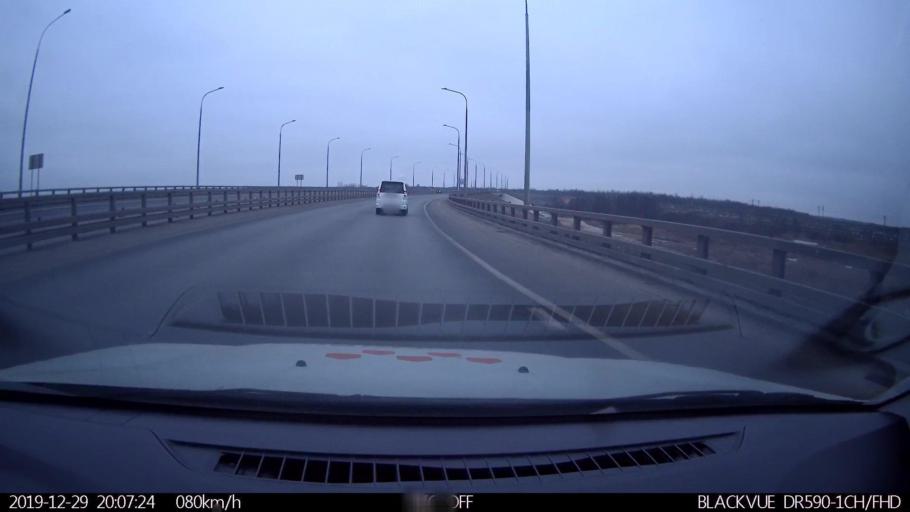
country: RU
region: Nizjnij Novgorod
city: Neklyudovo
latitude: 56.3939
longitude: 43.9837
